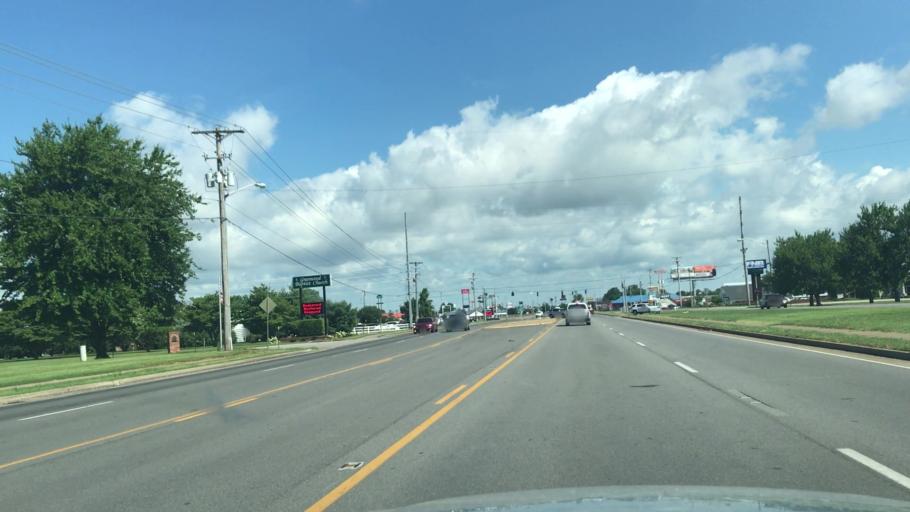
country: US
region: Kentucky
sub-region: Warren County
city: Plano
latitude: 36.9247
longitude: -86.4107
